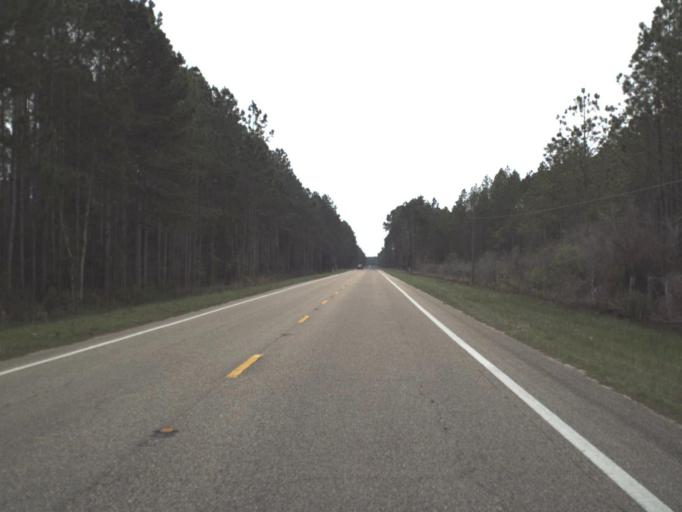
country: US
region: Florida
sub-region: Gulf County
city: Port Saint Joe
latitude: 29.8520
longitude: -85.2554
